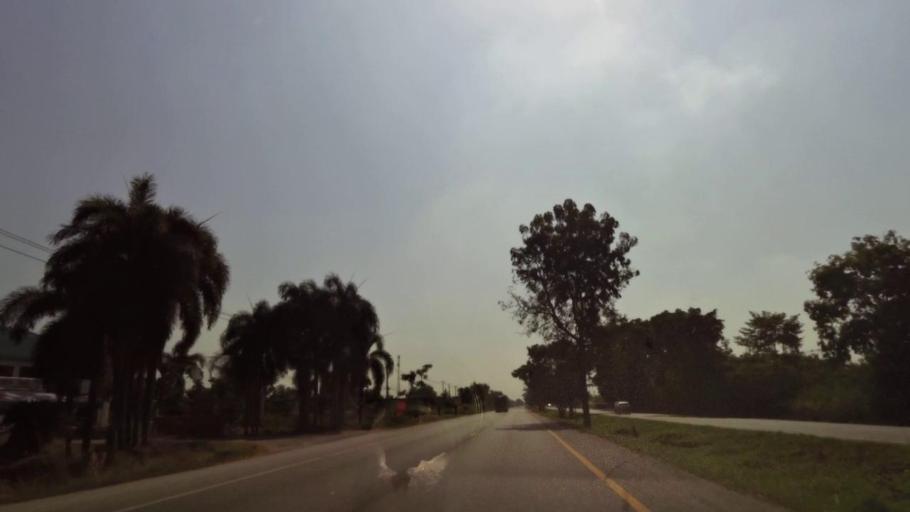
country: TH
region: Phichit
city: Bueng Na Rang
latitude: 16.3109
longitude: 100.1286
